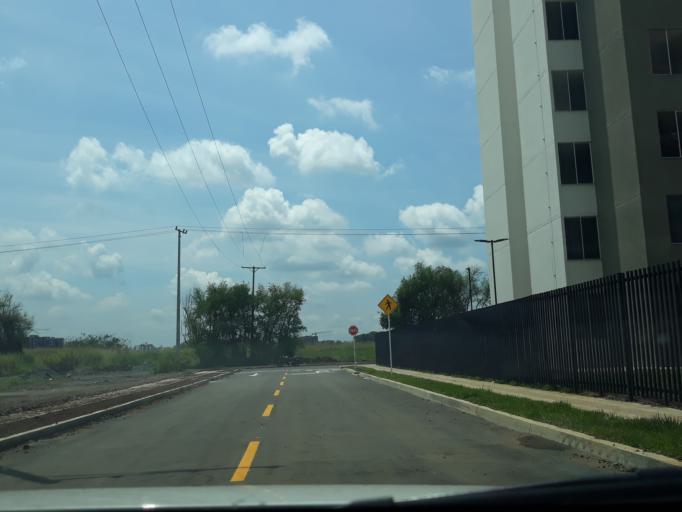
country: CO
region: Valle del Cauca
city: Cali
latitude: 3.3784
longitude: -76.5080
